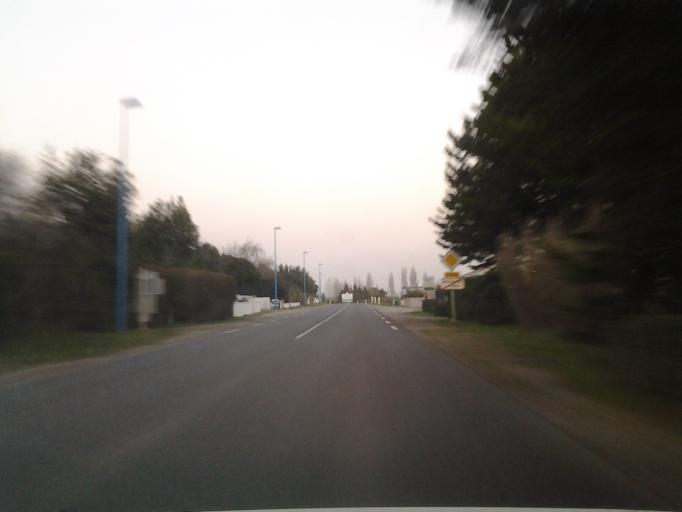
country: FR
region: Pays de la Loire
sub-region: Departement de la Vendee
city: Beauvoir-sur-Mer
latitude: 46.9061
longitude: -2.0244
